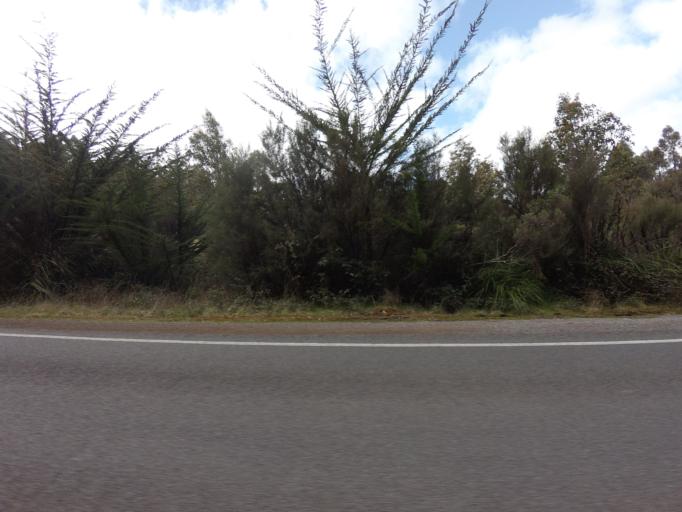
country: AU
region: Tasmania
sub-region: Huon Valley
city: Geeveston
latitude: -43.4083
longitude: 146.9588
